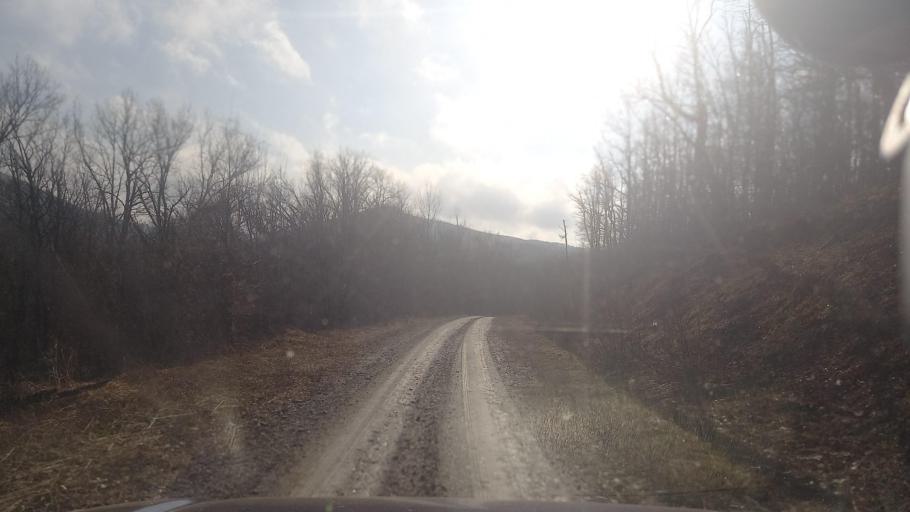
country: RU
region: Krasnodarskiy
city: Smolenskaya
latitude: 44.6858
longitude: 38.7842
